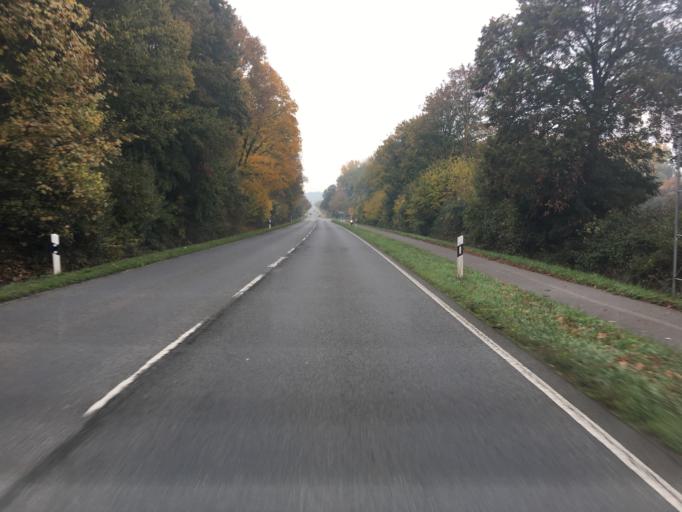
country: DE
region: North Rhine-Westphalia
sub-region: Regierungsbezirk Dusseldorf
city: Xanten
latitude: 51.6452
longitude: 6.4311
